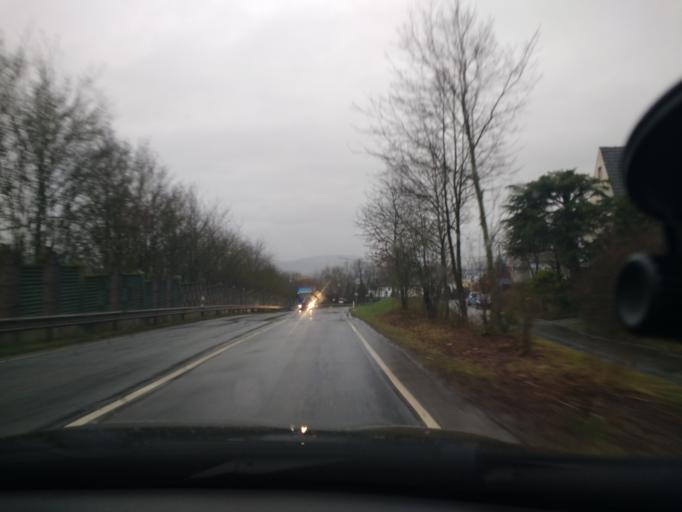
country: DE
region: Rheinland-Pfalz
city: Trier
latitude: 49.7216
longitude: 6.6295
